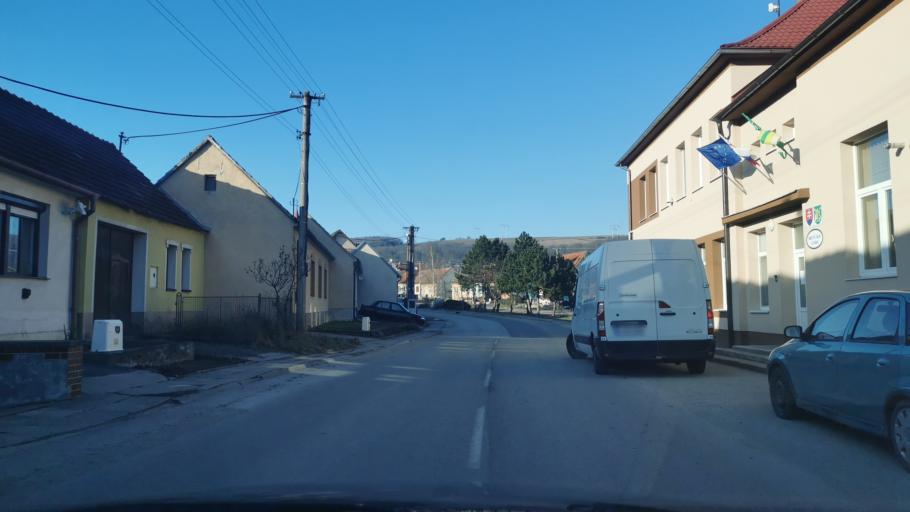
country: SK
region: Trnavsky
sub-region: Okres Senica
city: Senica
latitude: 48.7465
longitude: 17.3539
